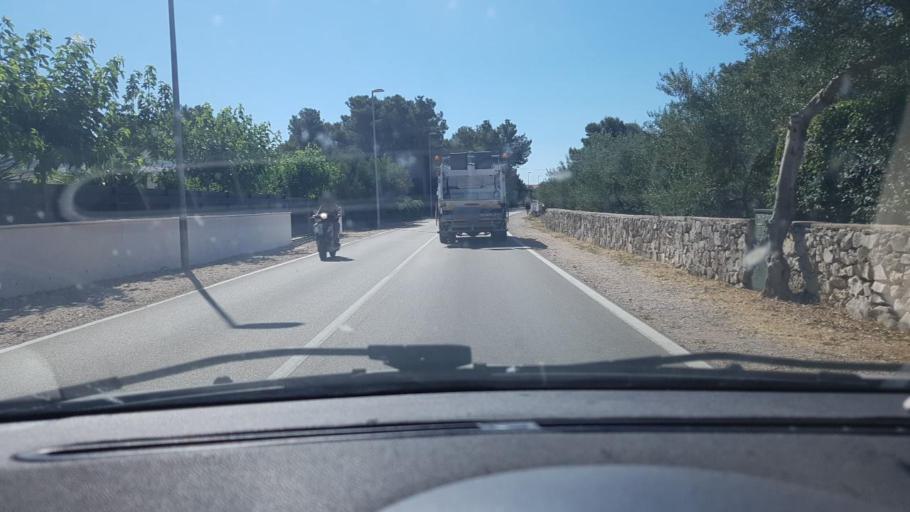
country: HR
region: Sibensko-Kniniska
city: Vodice
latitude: 43.7497
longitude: 15.7978
